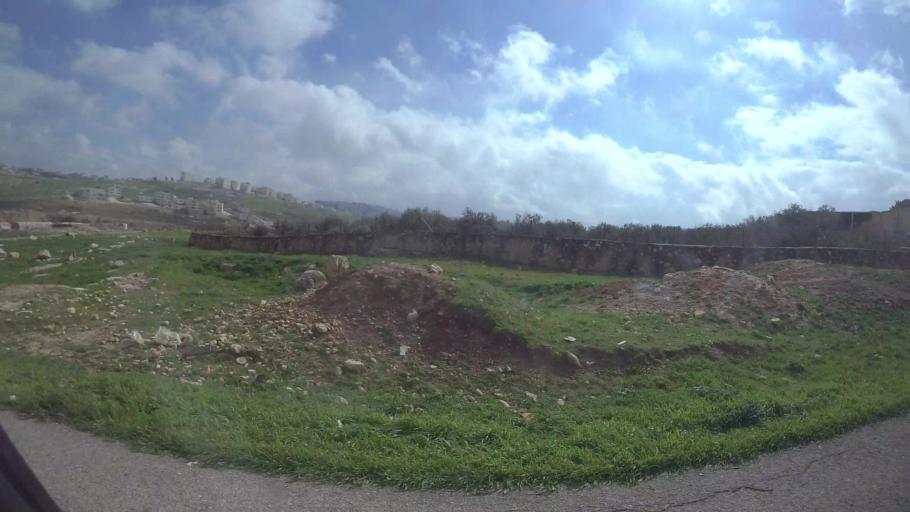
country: JO
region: Amman
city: Al Jubayhah
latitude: 32.0769
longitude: 35.8875
